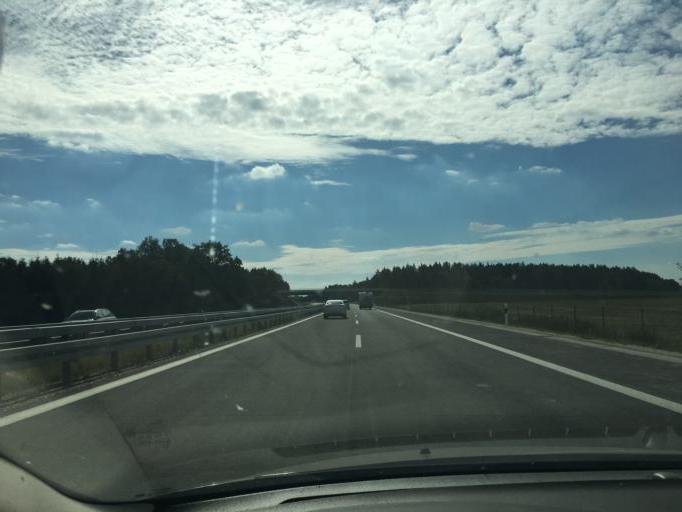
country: DE
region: Mecklenburg-Vorpommern
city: Gross Laasch
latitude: 53.3618
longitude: 11.5156
